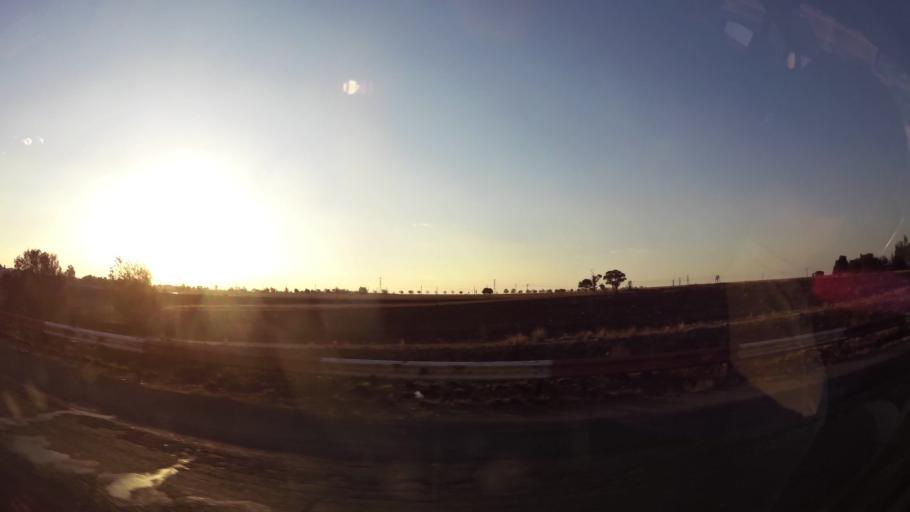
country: ZA
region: Gauteng
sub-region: West Rand District Municipality
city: Randfontein
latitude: -26.2044
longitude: 27.6657
